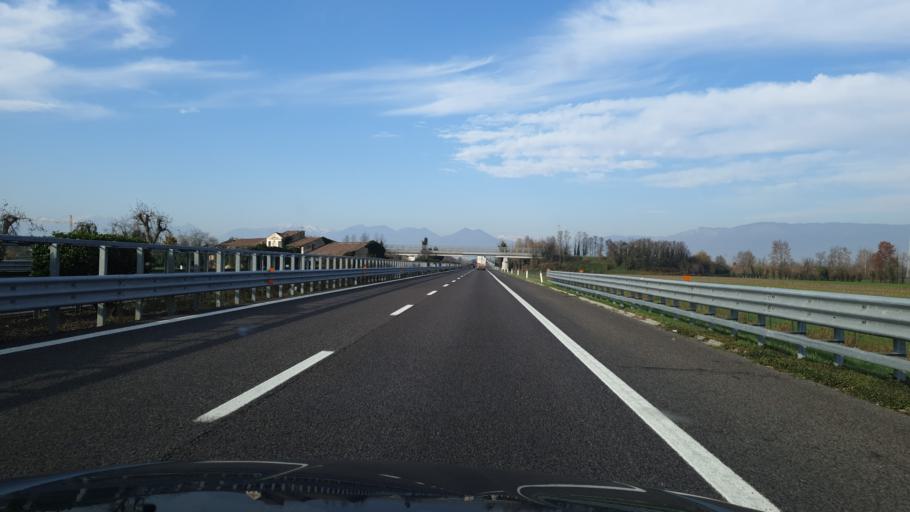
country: IT
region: Veneto
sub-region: Provincia di Vicenza
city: Dueville
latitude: 45.6328
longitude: 11.5830
